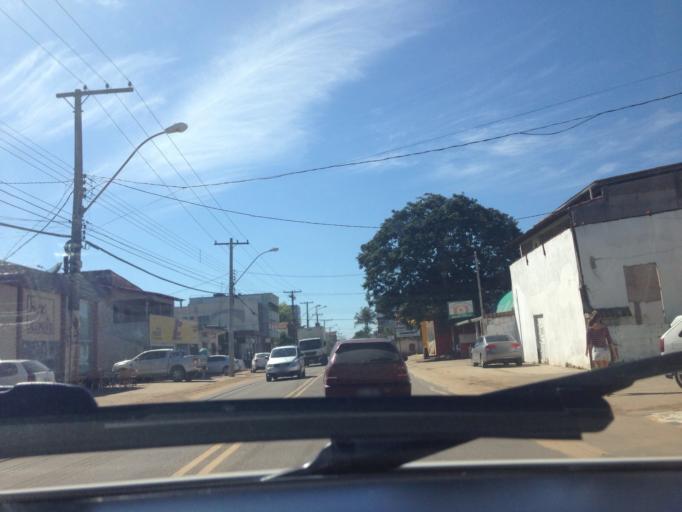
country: BR
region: Espirito Santo
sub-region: Guarapari
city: Guarapari
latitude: -20.6233
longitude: -40.4667
